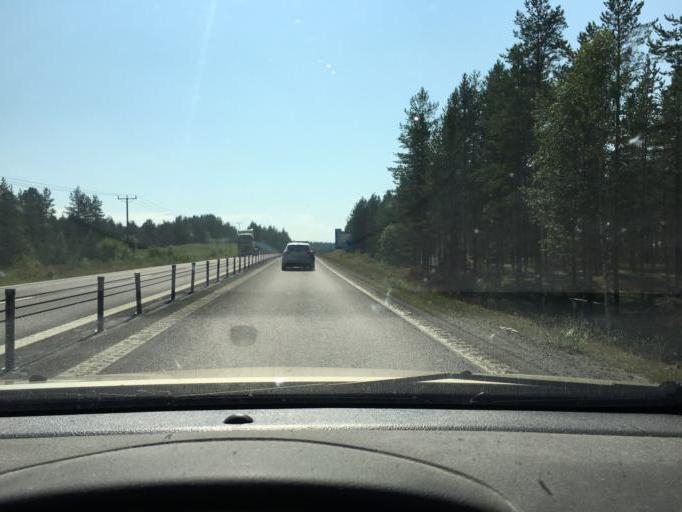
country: SE
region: Norrbotten
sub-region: Lulea Kommun
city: Gammelstad
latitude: 65.6036
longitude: 22.0505
